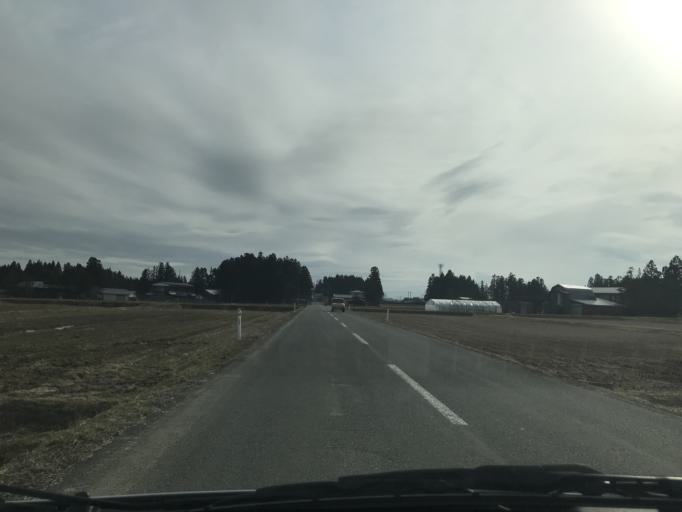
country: JP
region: Iwate
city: Hanamaki
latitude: 39.4097
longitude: 141.0785
